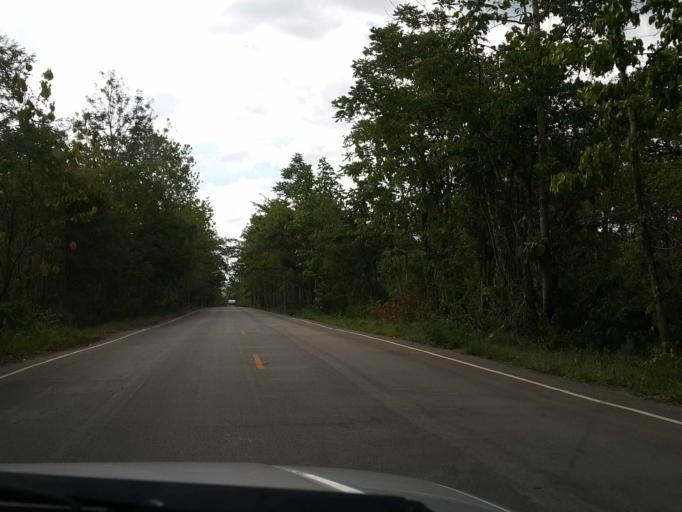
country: TH
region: Sukhothai
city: Thung Saliam
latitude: 17.3926
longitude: 99.3949
